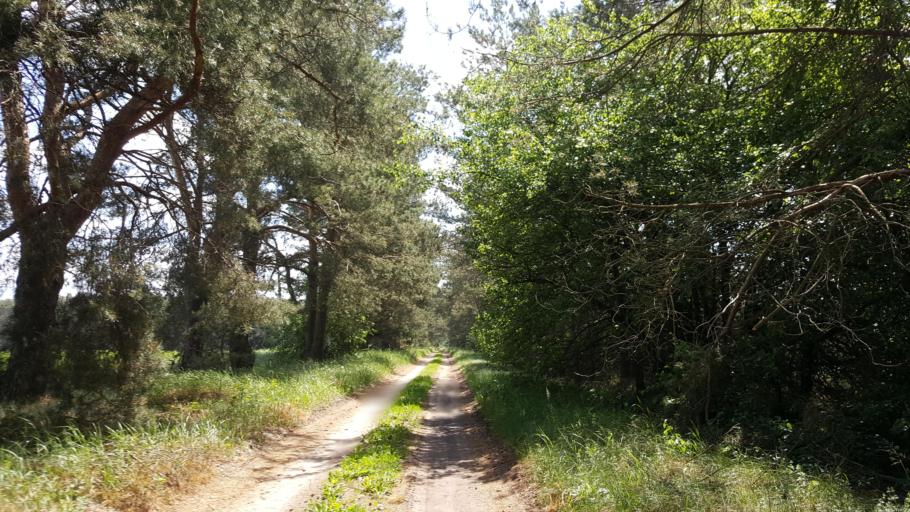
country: BY
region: Brest
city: Kamyanyets
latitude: 52.3960
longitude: 23.8614
